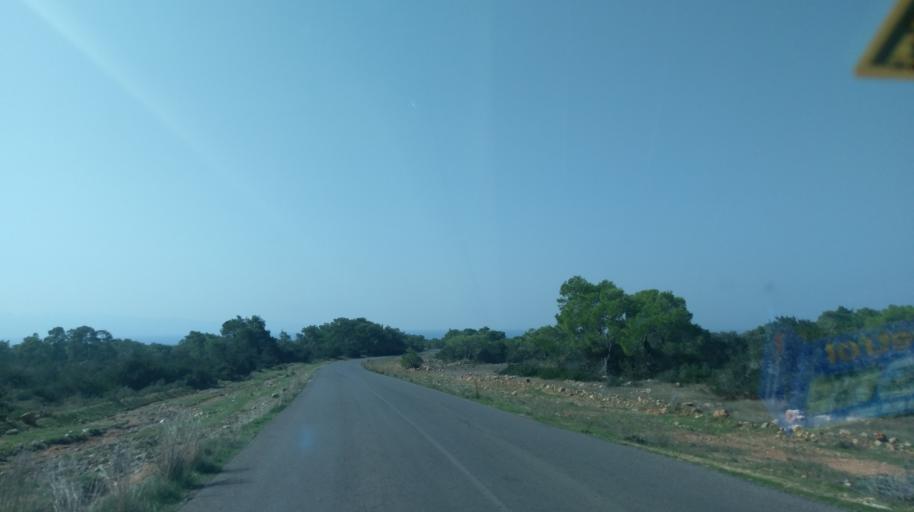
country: CY
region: Lefkosia
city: Morfou
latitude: 35.3015
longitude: 32.9913
